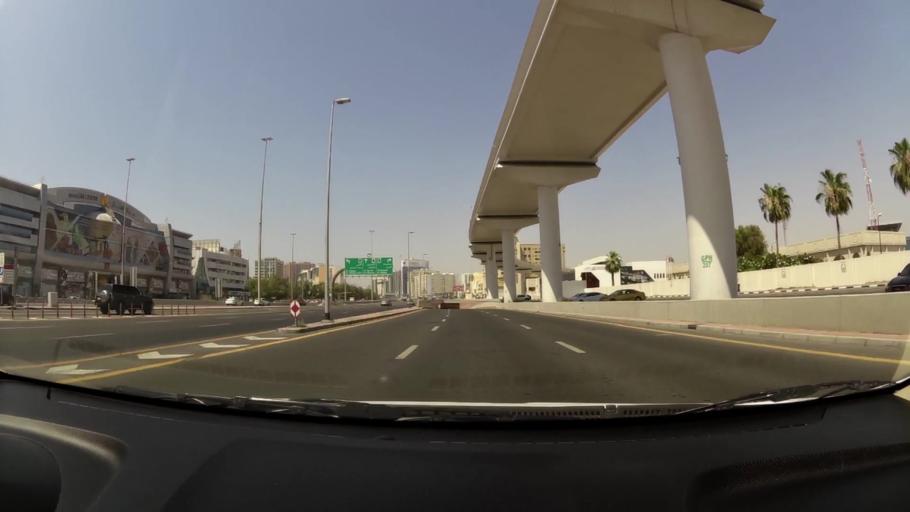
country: AE
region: Ash Shariqah
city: Sharjah
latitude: 25.2788
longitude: 55.3540
